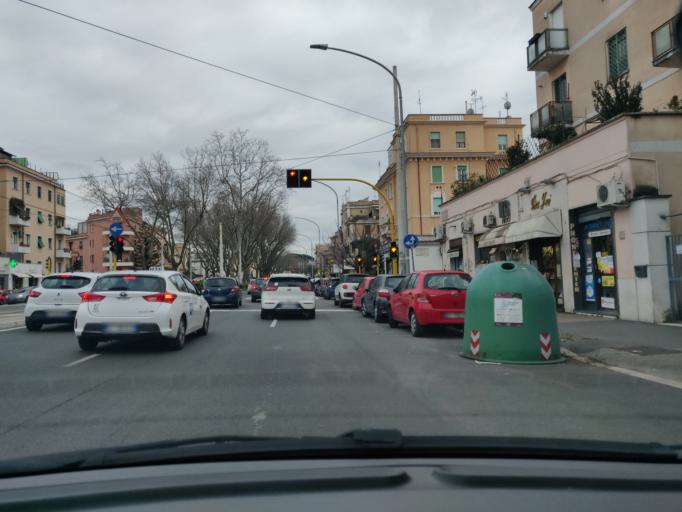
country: VA
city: Vatican City
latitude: 41.8742
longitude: 12.4469
